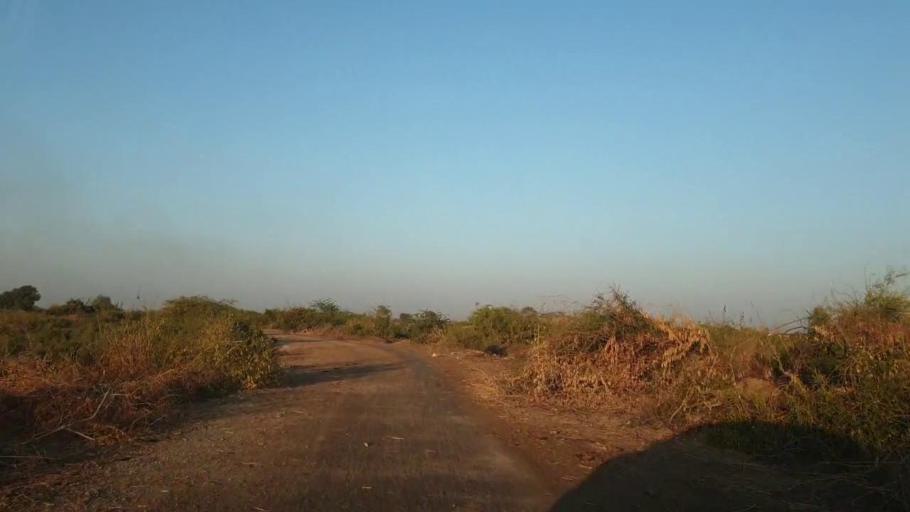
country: PK
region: Sindh
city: Mirpur Khas
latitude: 25.7157
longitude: 69.0627
